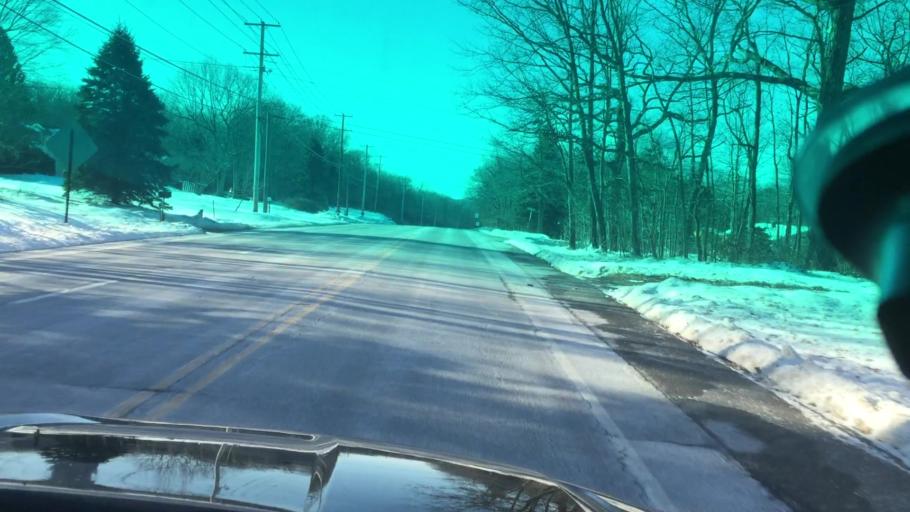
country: US
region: Pennsylvania
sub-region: Luzerne County
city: Oakdale
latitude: 41.0172
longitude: -75.9228
